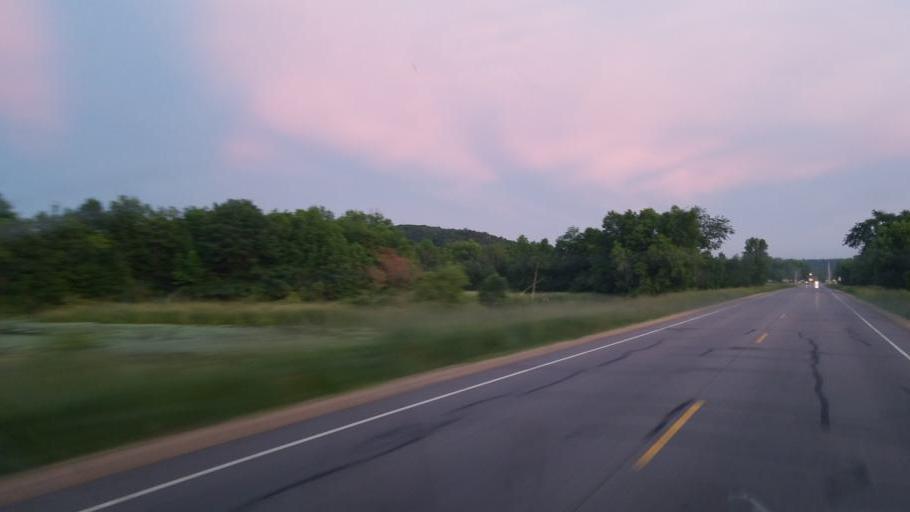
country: US
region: Wisconsin
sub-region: Juneau County
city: Elroy
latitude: 43.6928
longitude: -90.2663
